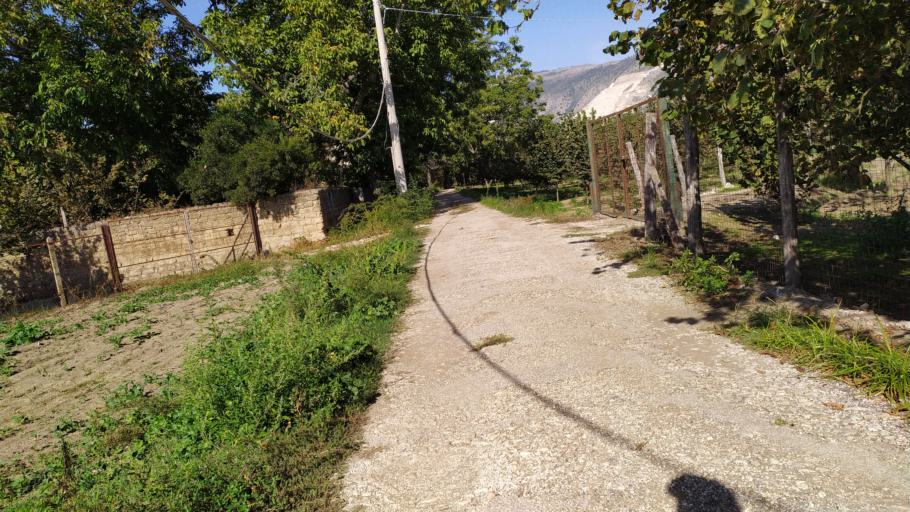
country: IT
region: Campania
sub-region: Provincia di Napoli
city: Camposano
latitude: 40.9630
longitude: 14.5183
